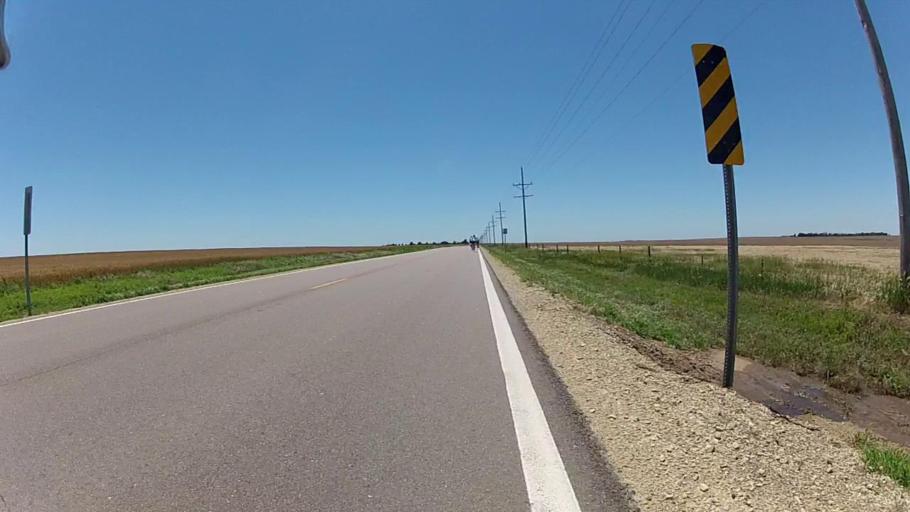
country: US
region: Kansas
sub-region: Kiowa County
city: Greensburg
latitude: 37.5275
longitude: -99.3207
